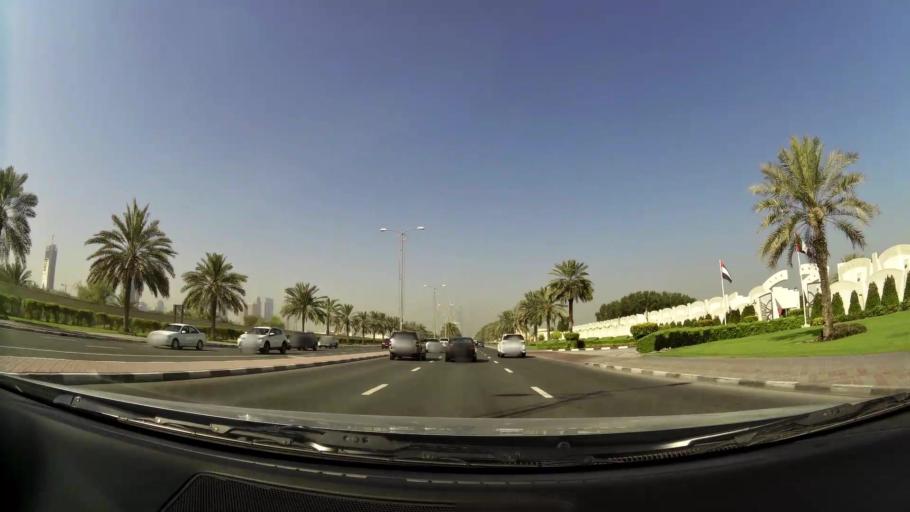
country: AE
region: Dubai
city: Dubai
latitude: 25.1207
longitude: 55.1768
